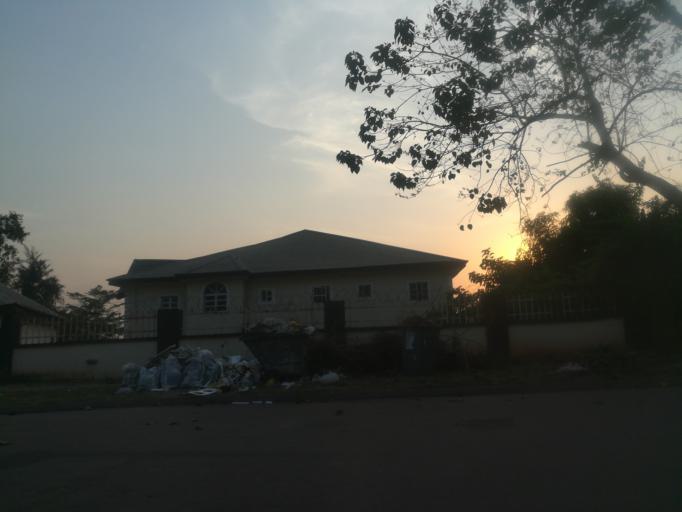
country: NG
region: Abuja Federal Capital Territory
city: Abuja
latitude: 9.0632
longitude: 7.4380
